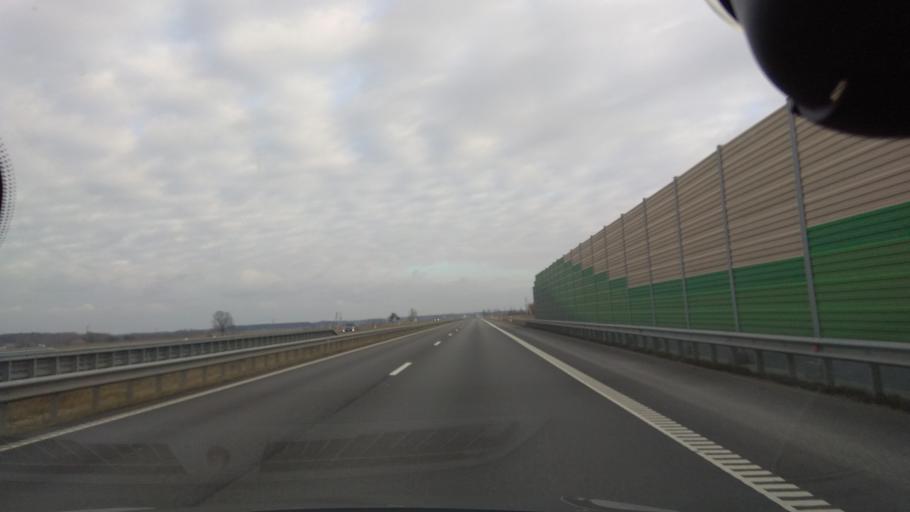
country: LT
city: Kazlu Ruda
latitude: 54.6828
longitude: 23.5858
